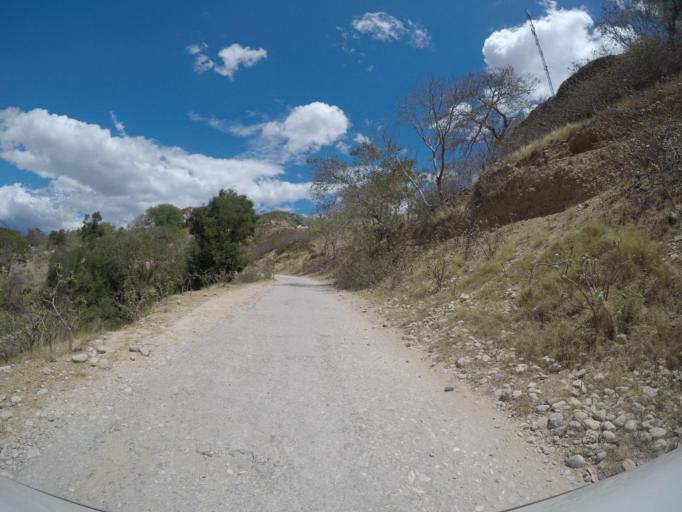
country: TL
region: Baucau
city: Baucau
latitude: -8.4740
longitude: 126.6011
